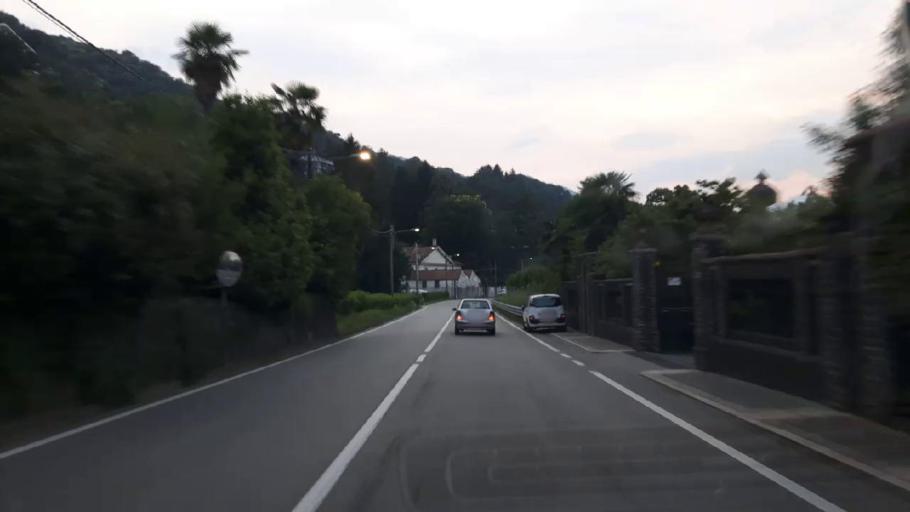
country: IT
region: Piedmont
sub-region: Provincia Verbano-Cusio-Ossola
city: Stresa
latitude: 45.8901
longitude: 8.5210
